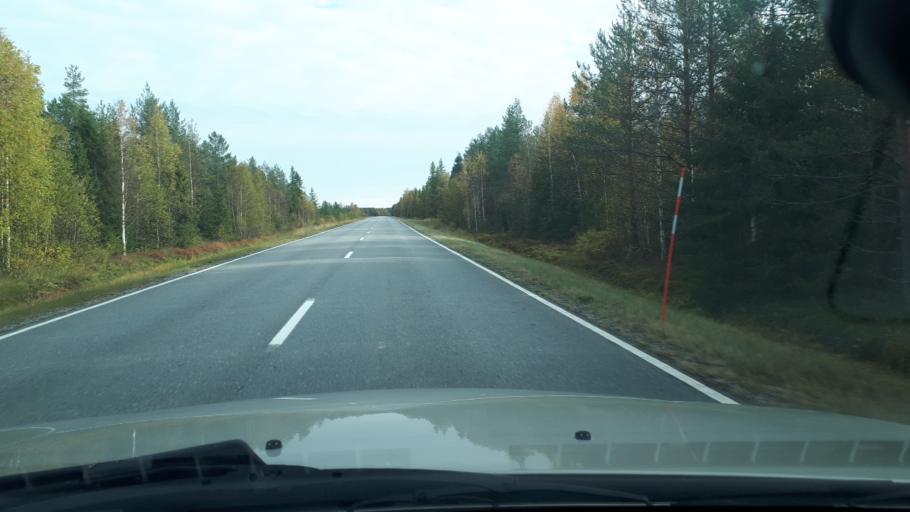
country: FI
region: Lapland
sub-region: Rovaniemi
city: Ranua
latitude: 65.9801
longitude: 26.1349
